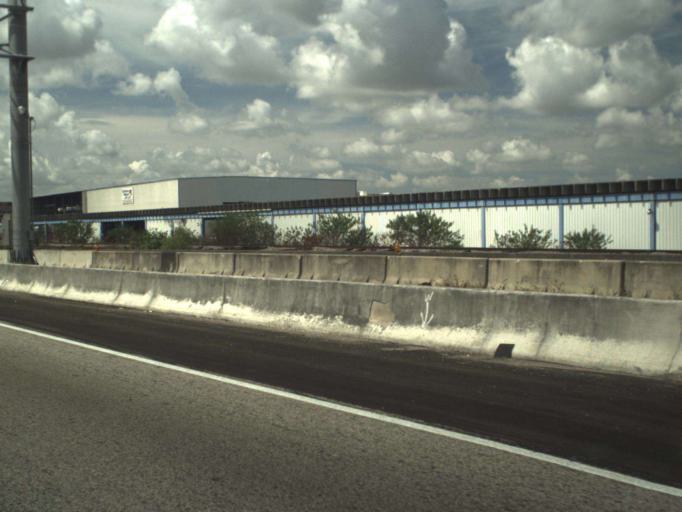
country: US
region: Florida
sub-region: Broward County
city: Dania Beach
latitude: 26.0678
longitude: -80.1656
